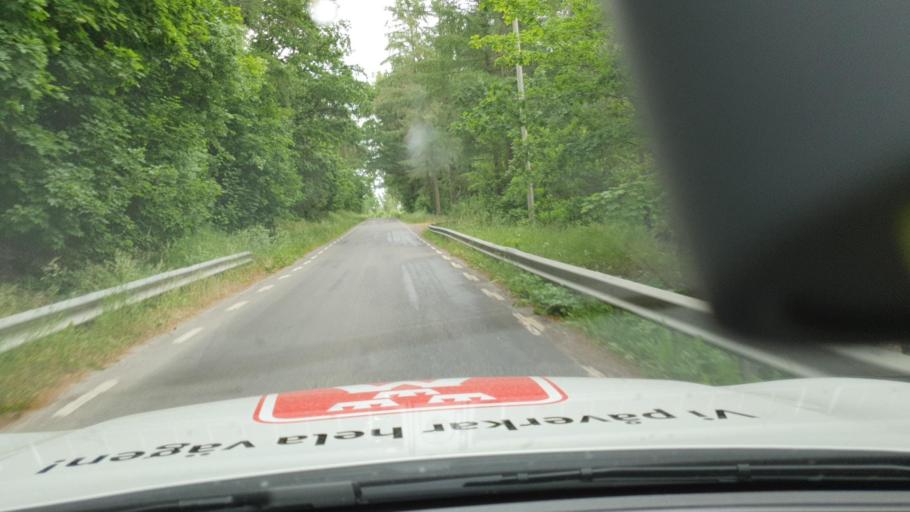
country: SE
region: Vaestra Goetaland
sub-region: Tibro Kommun
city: Tibro
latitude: 58.3226
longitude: 14.0980
